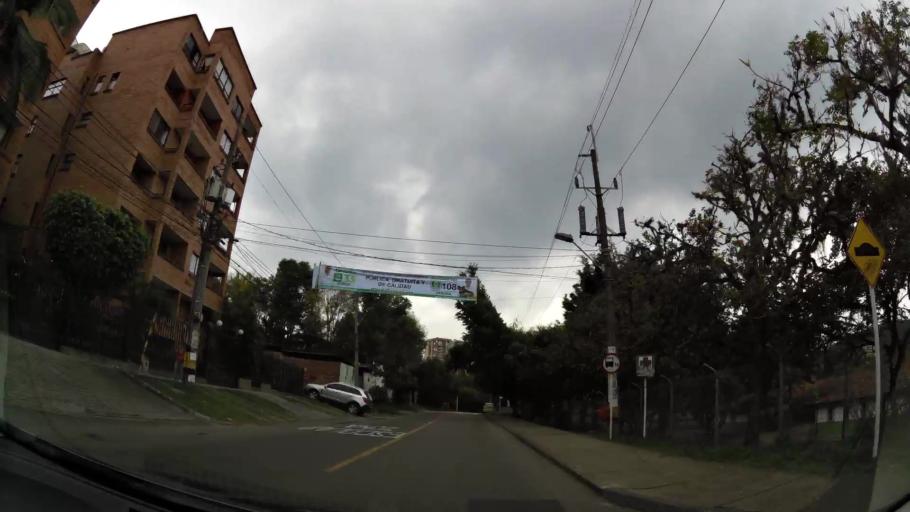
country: CO
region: Antioquia
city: Medellin
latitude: 6.2764
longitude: -75.5884
